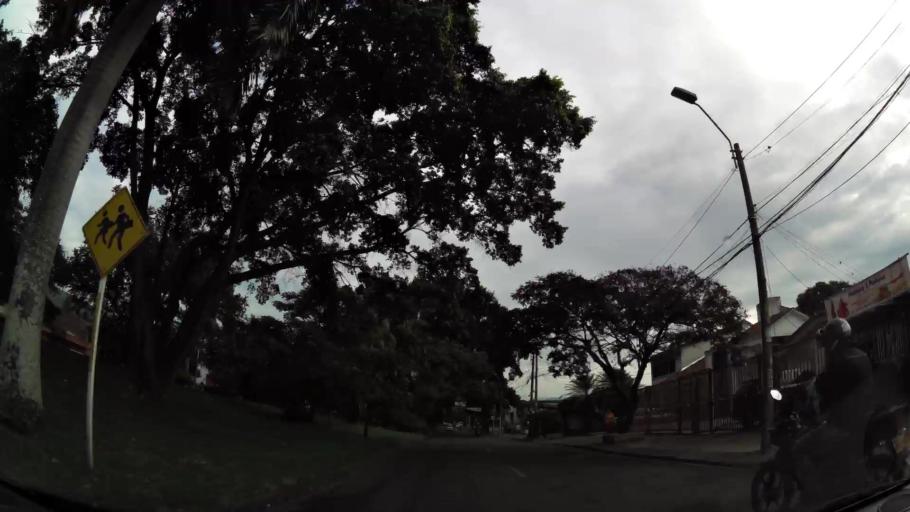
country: CO
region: Valle del Cauca
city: Cali
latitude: 3.4859
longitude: -76.5200
